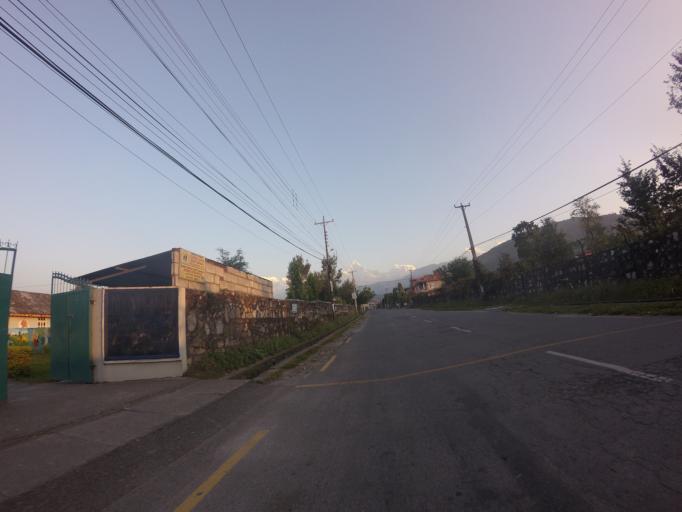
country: NP
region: Western Region
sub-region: Gandaki Zone
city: Pokhara
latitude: 28.2157
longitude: 83.9979
